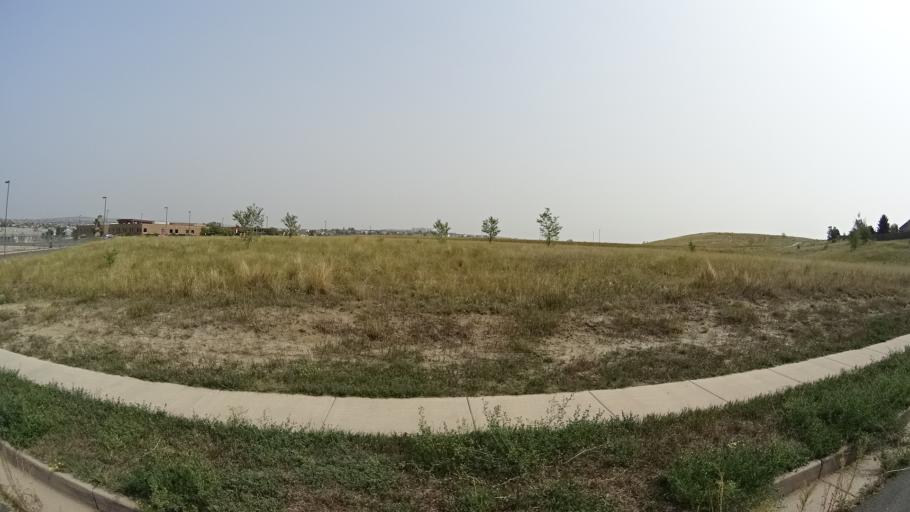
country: US
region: Colorado
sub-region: El Paso County
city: Cimarron Hills
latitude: 38.9263
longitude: -104.7447
